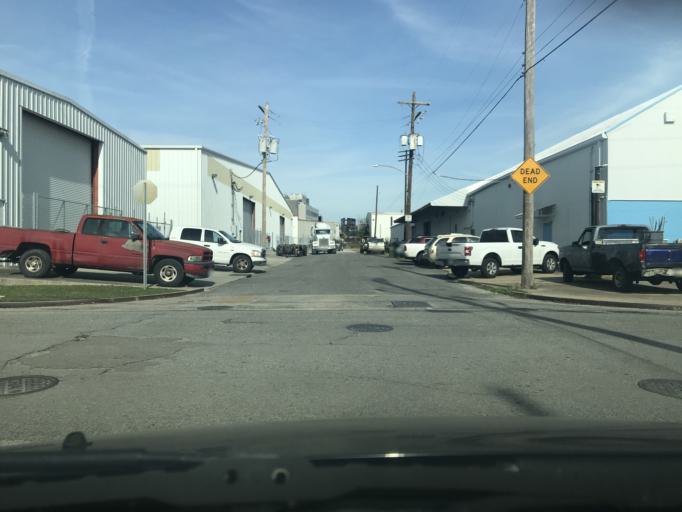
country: US
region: Louisiana
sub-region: Orleans Parish
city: New Orleans
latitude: 29.9578
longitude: -90.0990
